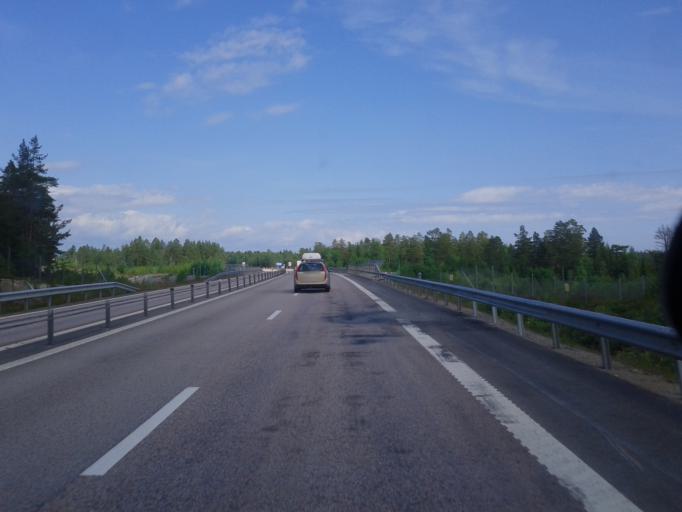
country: SE
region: Vaesternorrland
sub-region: OErnskoeldsviks Kommun
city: Husum
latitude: 63.3676
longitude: 19.1864
